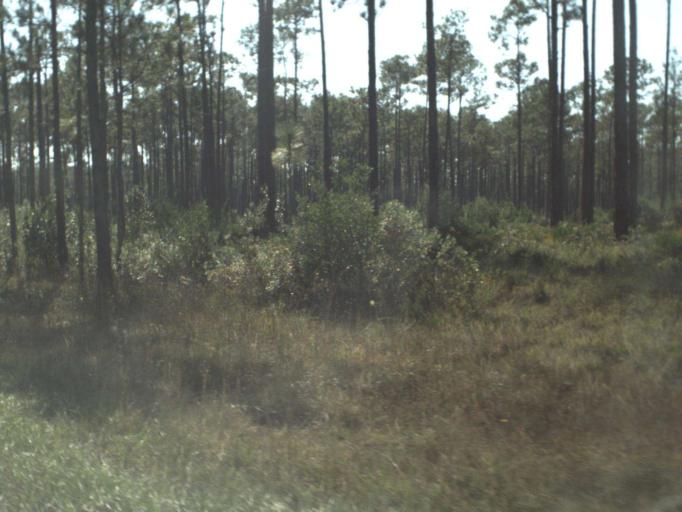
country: US
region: Florida
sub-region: Gulf County
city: Wewahitchka
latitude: 30.1032
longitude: -84.9860
